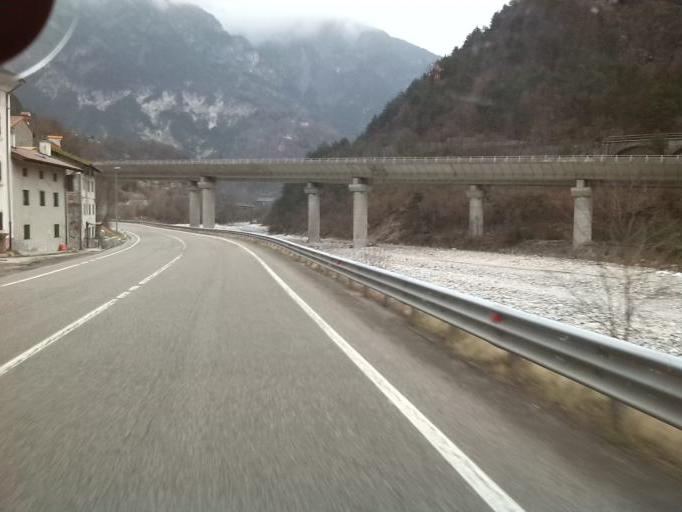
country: IT
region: Friuli Venezia Giulia
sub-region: Provincia di Udine
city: Dogna
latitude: 46.4380
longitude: 13.3089
